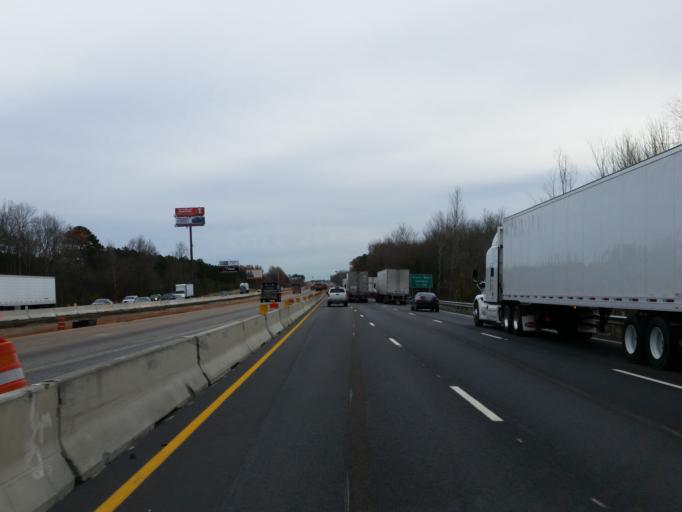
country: US
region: Georgia
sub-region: Henry County
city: McDonough
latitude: 33.4460
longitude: -84.1989
